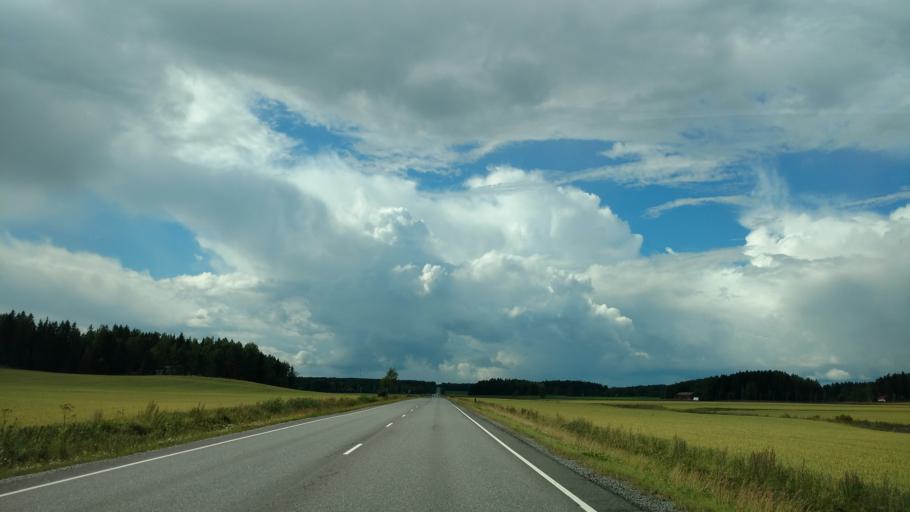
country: FI
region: Varsinais-Suomi
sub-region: Turku
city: Sauvo
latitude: 60.3899
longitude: 22.8729
